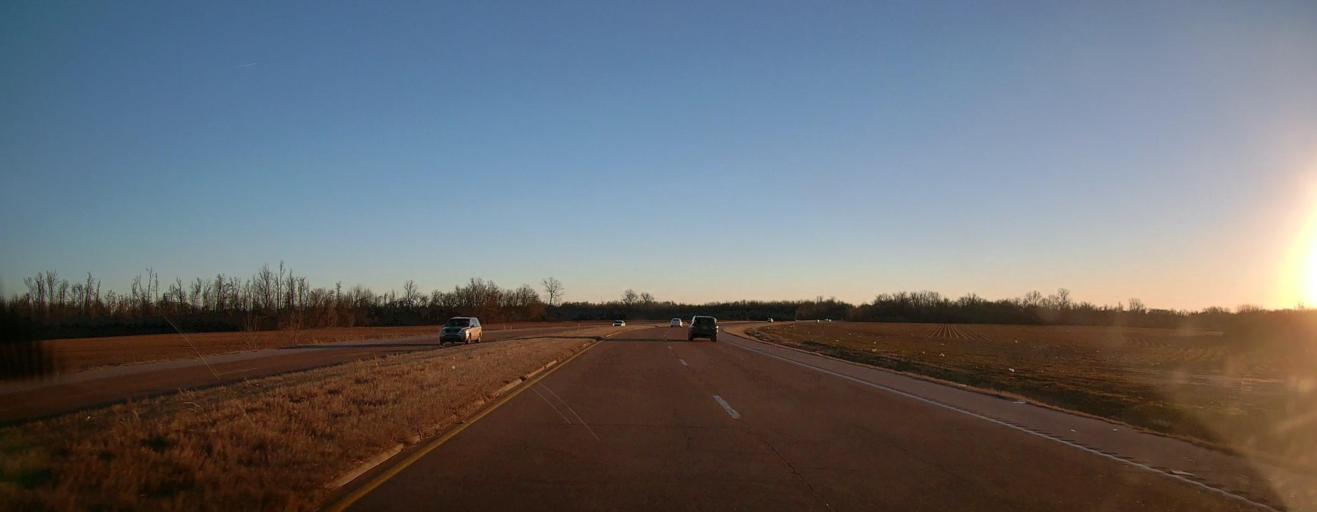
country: US
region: Tennessee
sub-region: Shelby County
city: Millington
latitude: 35.2887
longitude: -89.8820
